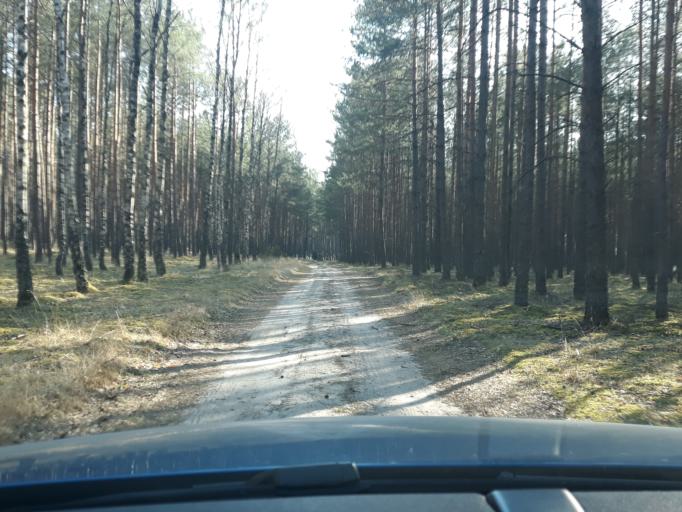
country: PL
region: Pomeranian Voivodeship
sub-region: Powiat bytowski
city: Lipnica
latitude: 53.9069
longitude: 17.4965
